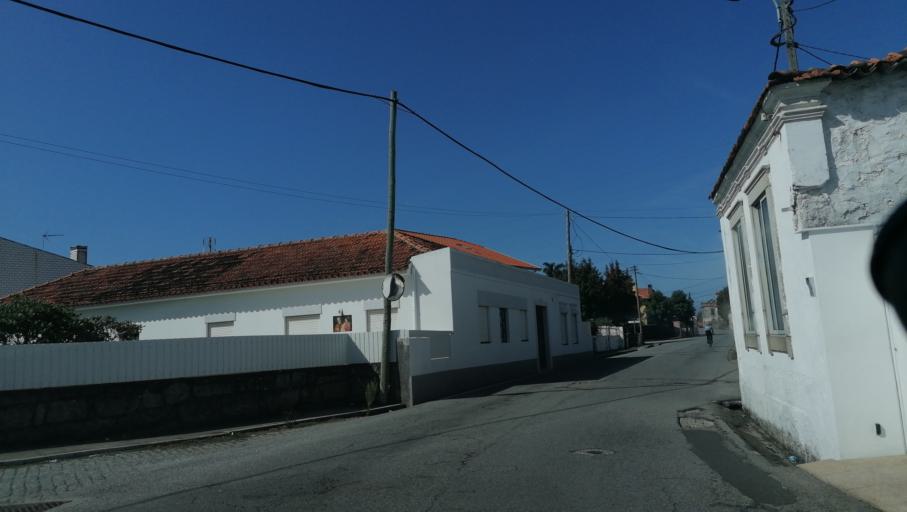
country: PT
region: Aveiro
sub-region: Espinho
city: Silvalde
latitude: 41.0018
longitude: -8.6212
